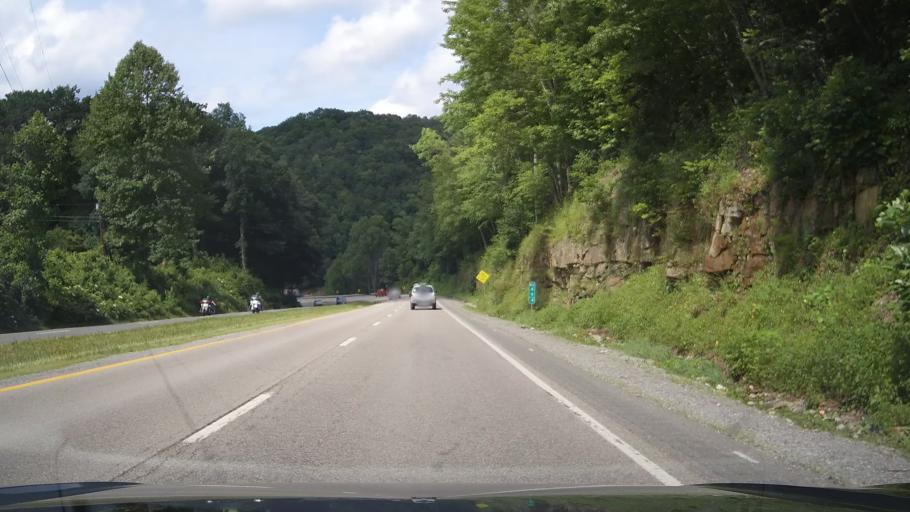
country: US
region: Virginia
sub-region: Wise County
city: Wise
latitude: 37.0173
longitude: -82.5899
